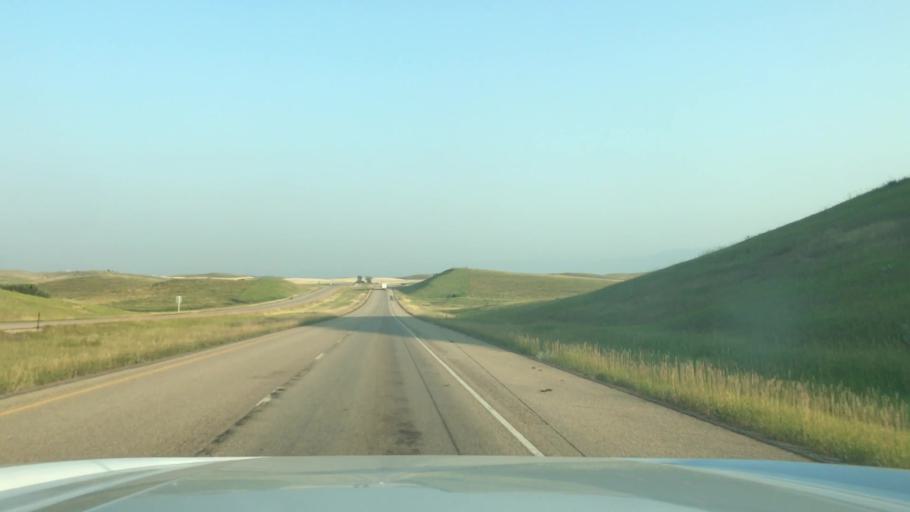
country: US
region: Wyoming
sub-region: Sheridan County
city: Sheridan
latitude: 45.0143
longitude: -107.3056
